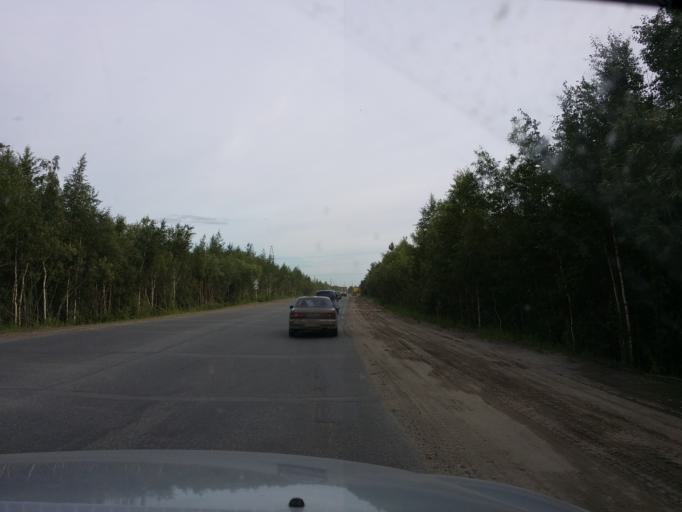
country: RU
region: Khanty-Mansiyskiy Avtonomnyy Okrug
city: Nizhnevartovsk
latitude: 60.9622
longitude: 76.6621
